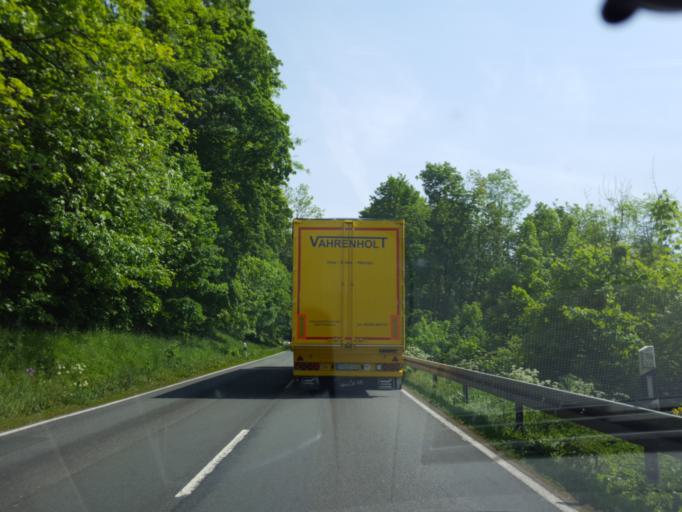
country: DE
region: North Rhine-Westphalia
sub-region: Regierungsbezirk Arnsberg
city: Olsberg
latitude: 51.3796
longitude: 8.4749
